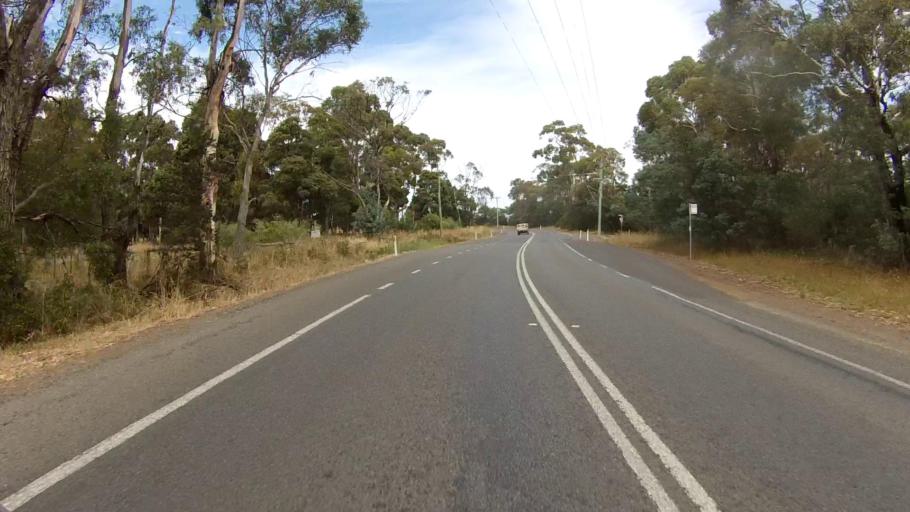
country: AU
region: Tasmania
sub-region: Clarence
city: Sandford
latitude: -42.9289
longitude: 147.4918
